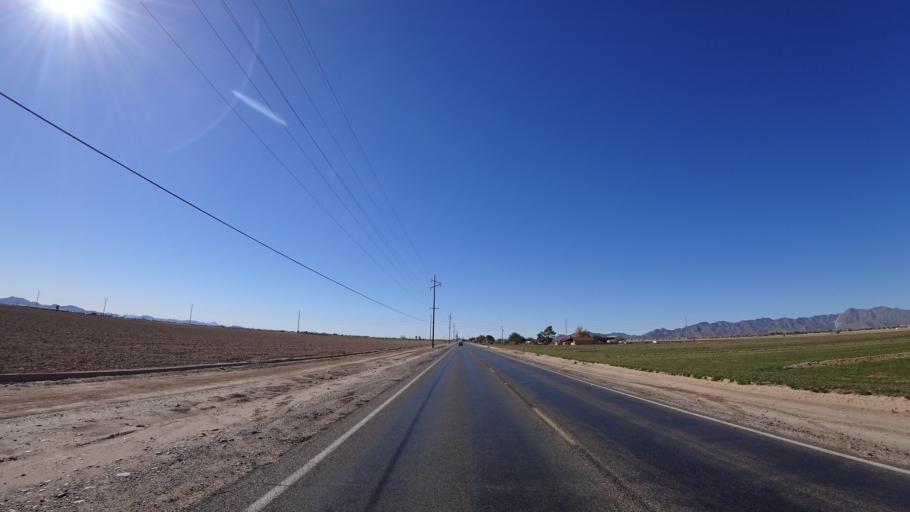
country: US
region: Arizona
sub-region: Maricopa County
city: Goodyear
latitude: 33.4356
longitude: -112.4548
